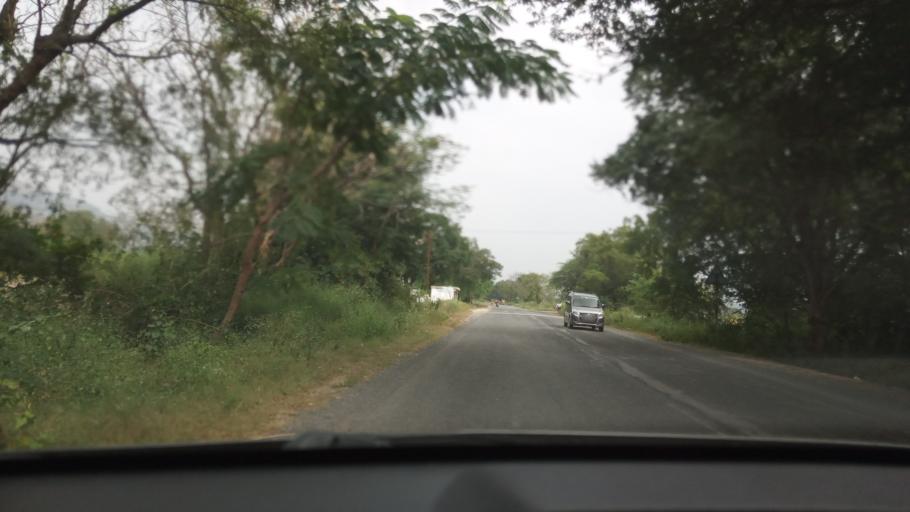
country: IN
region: Andhra Pradesh
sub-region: Chittoor
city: Madanapalle
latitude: 13.6518
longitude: 78.8299
